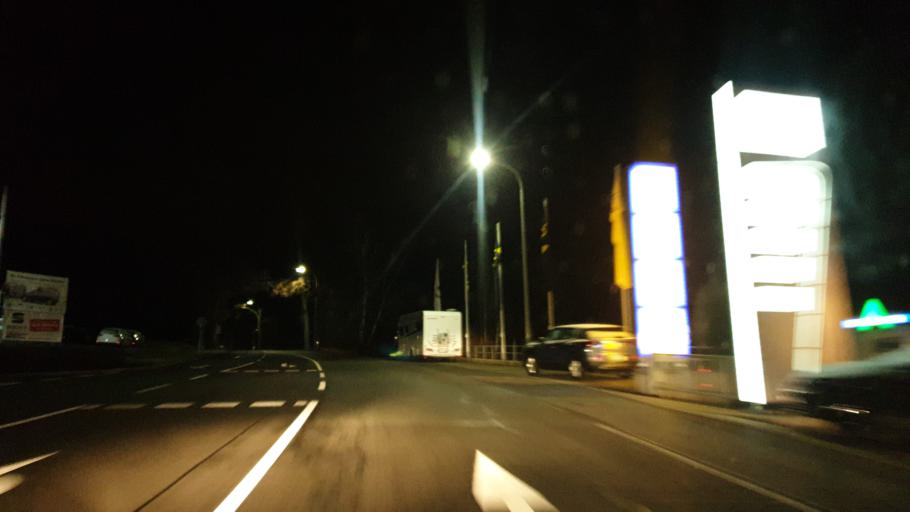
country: DE
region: Saxony
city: Oelsnitz
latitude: 50.7217
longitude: 12.7195
